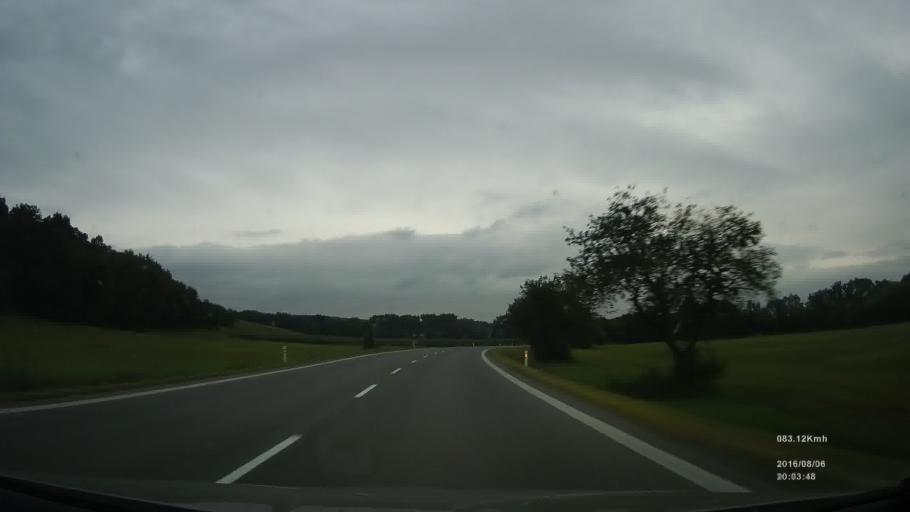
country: SK
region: Presovsky
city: Stropkov
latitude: 49.2462
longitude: 21.6143
